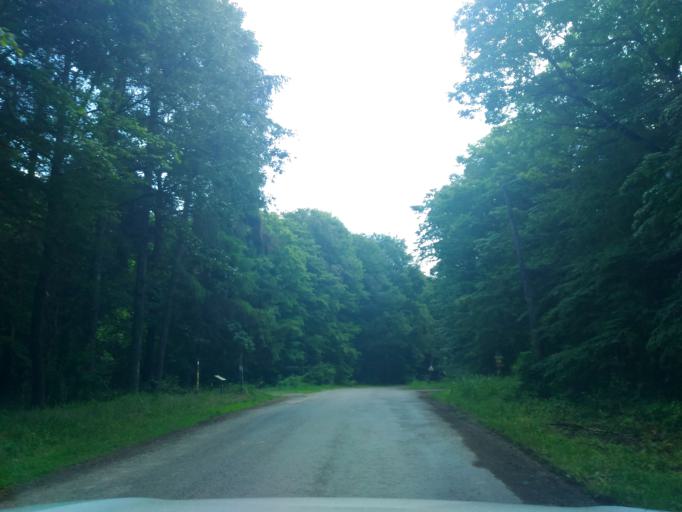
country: HU
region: Baranya
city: Pecs
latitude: 46.1249
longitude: 18.2201
